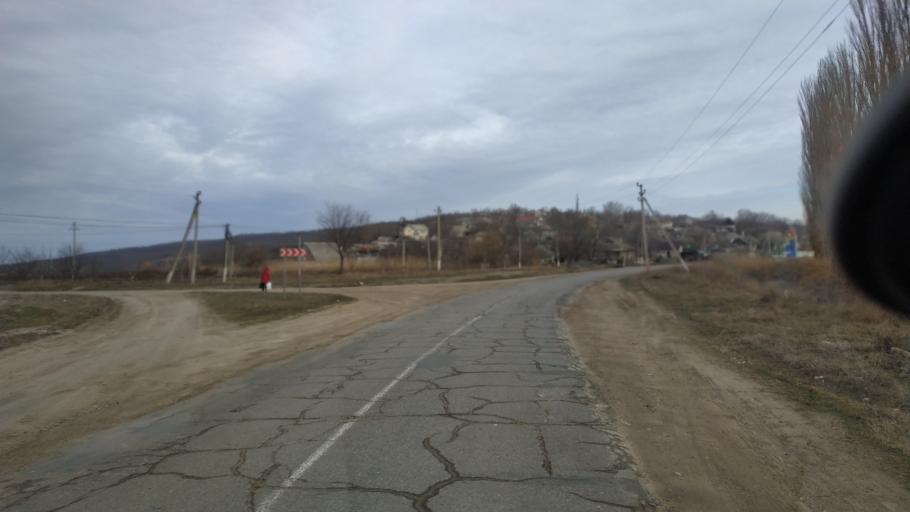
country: MD
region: Chisinau
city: Vadul lui Voda
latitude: 47.1385
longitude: 29.0611
